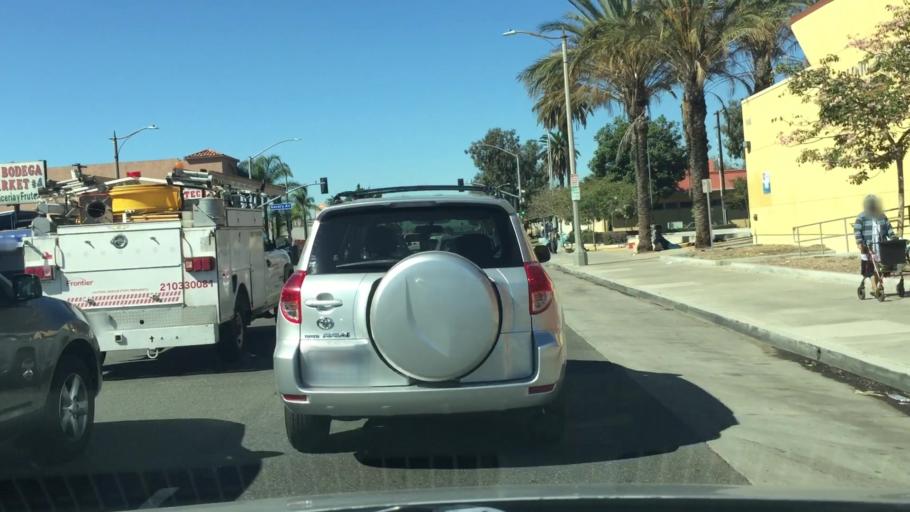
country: US
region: California
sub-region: Los Angeles County
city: Long Beach
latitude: 33.7827
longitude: -118.1733
